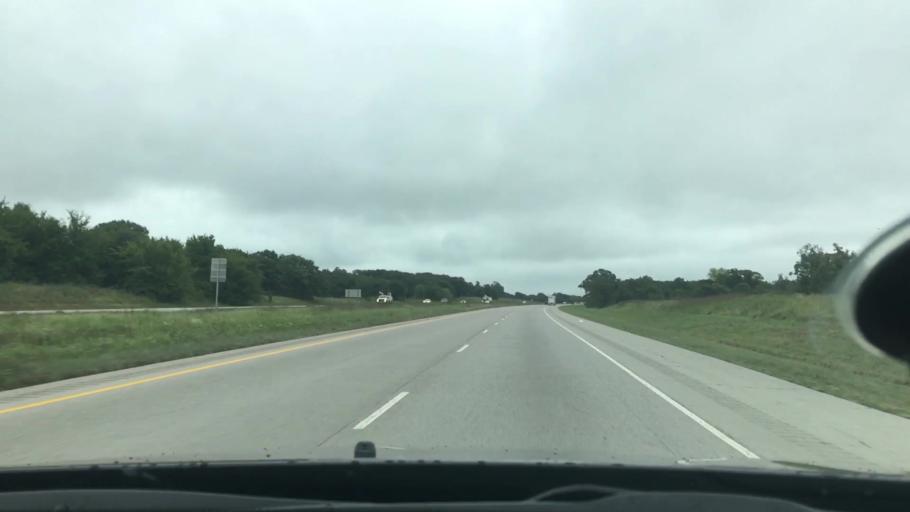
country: US
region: Oklahoma
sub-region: Okfuskee County
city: Okemah
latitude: 35.3977
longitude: -96.3921
